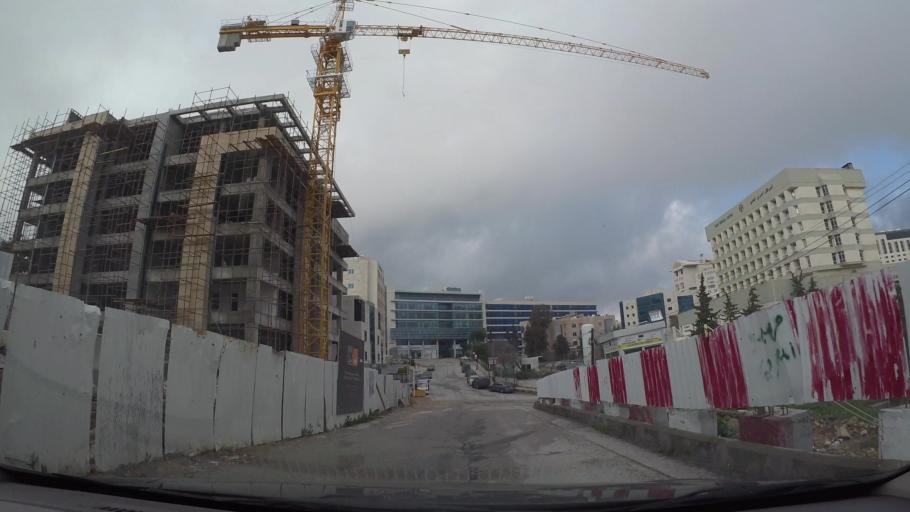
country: JO
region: Amman
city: Wadi as Sir
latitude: 31.9590
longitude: 35.8774
